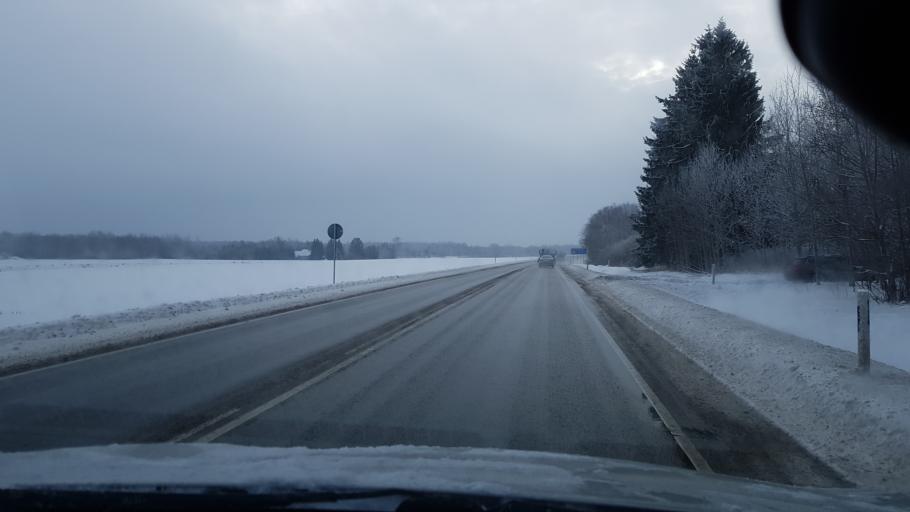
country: EE
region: Harju
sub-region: Saue linn
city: Saue
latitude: 59.3397
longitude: 24.4805
